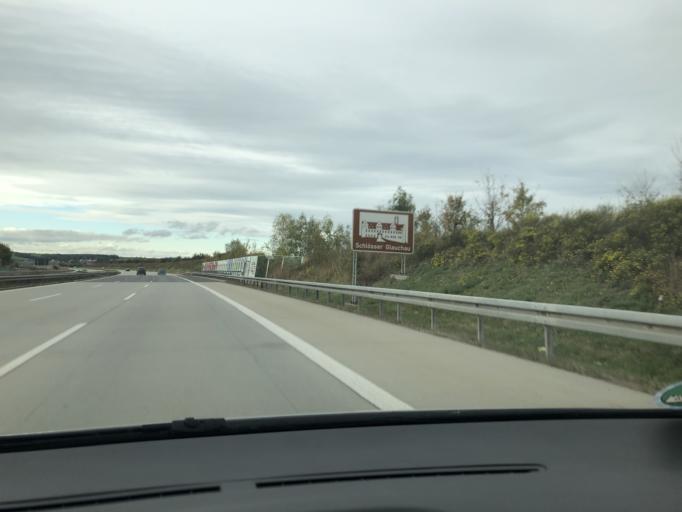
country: DE
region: Saxony
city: Remse
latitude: 50.8429
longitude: 12.5815
